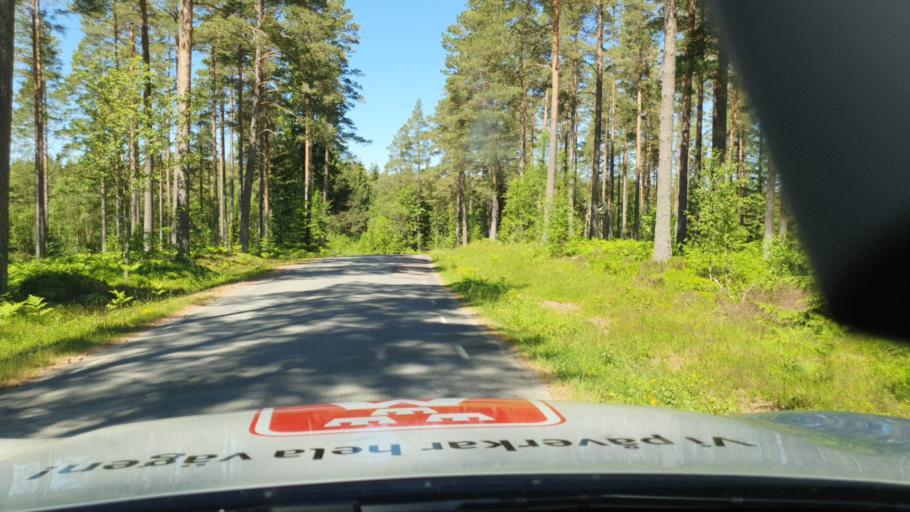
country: SE
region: Joenkoeping
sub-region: Habo Kommun
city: Habo
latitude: 57.8902
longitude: 13.9969
